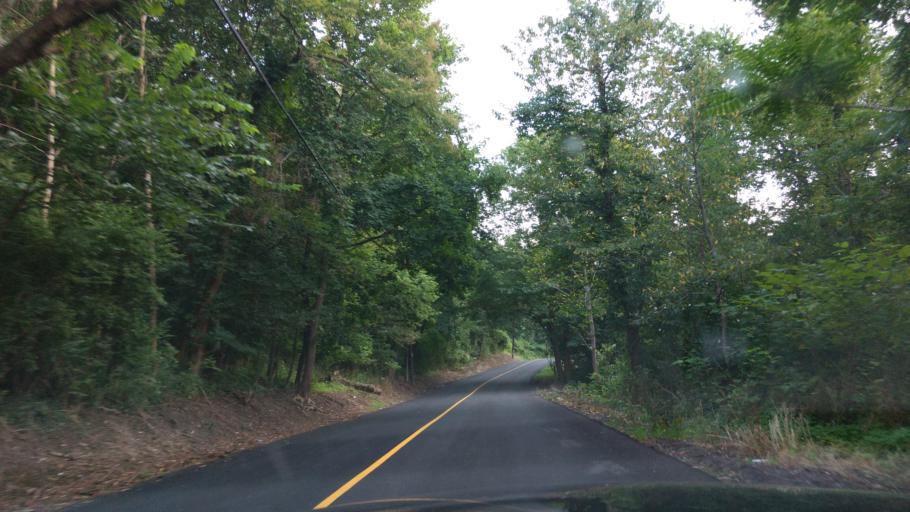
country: US
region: Pennsylvania
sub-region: Allegheny County
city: Bellevue
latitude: 40.4993
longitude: -80.0432
